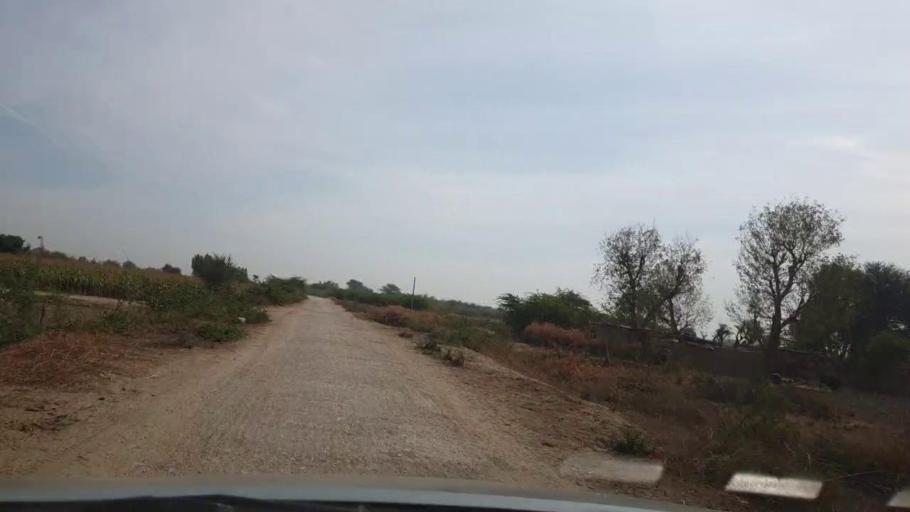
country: PK
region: Sindh
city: Kunri
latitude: 25.1613
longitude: 69.5930
